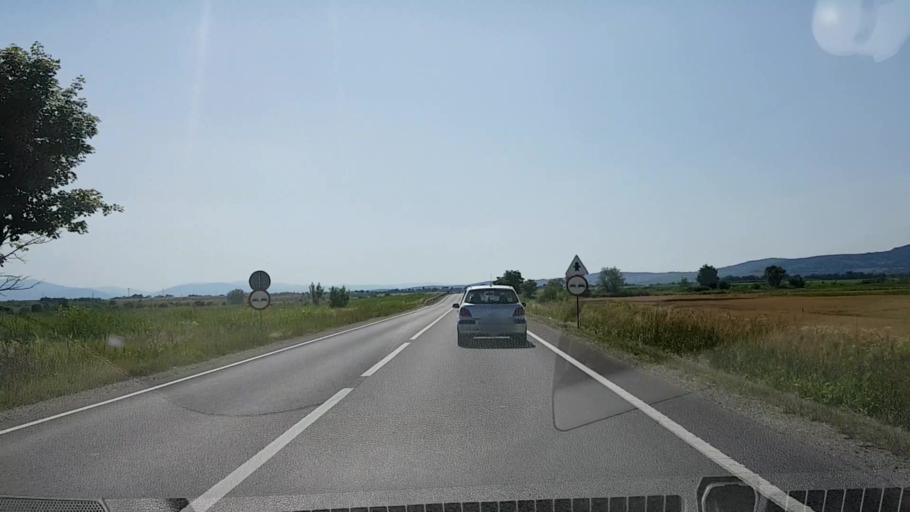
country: RO
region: Sibiu
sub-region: Comuna Porumbacu de Jos
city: Porumbacu de Jos
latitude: 45.7569
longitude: 24.4903
